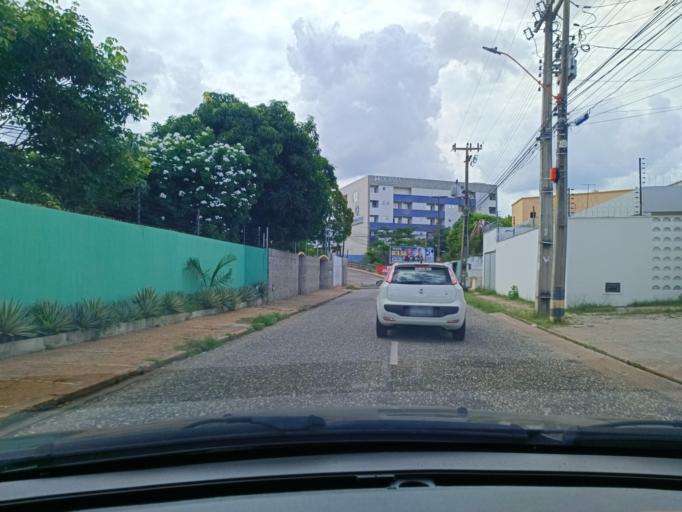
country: BR
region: Piaui
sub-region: Teresina
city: Teresina
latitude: -5.0887
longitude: -42.7997
